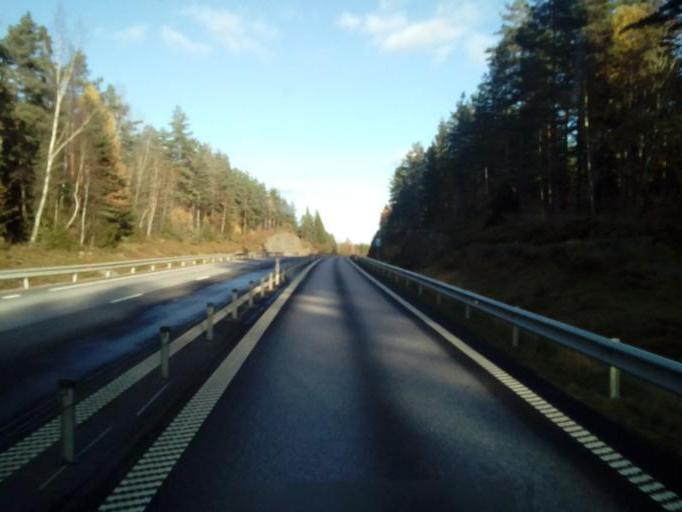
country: SE
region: Kalmar
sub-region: Vimmerby Kommun
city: Vimmerby
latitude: 57.7141
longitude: 16.0541
